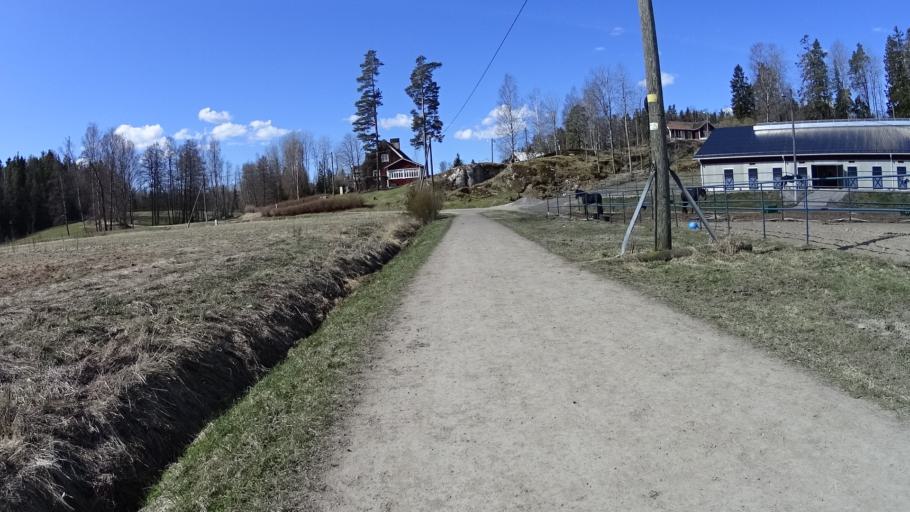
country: FI
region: Uusimaa
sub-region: Helsinki
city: Espoo
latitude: 60.2387
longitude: 24.6475
